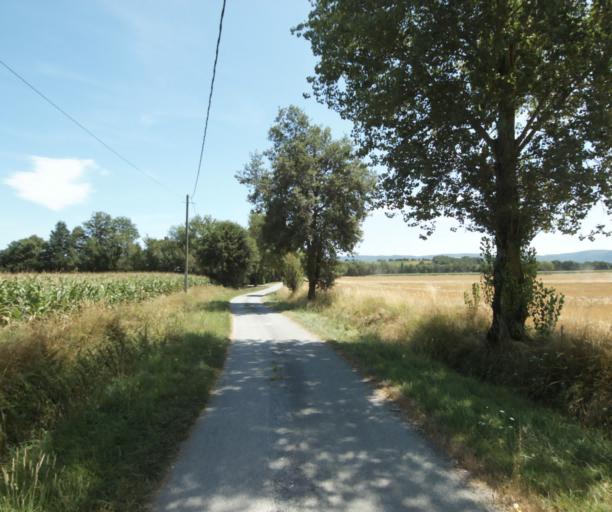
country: FR
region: Midi-Pyrenees
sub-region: Departement de la Haute-Garonne
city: Revel
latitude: 43.5020
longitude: 2.0380
